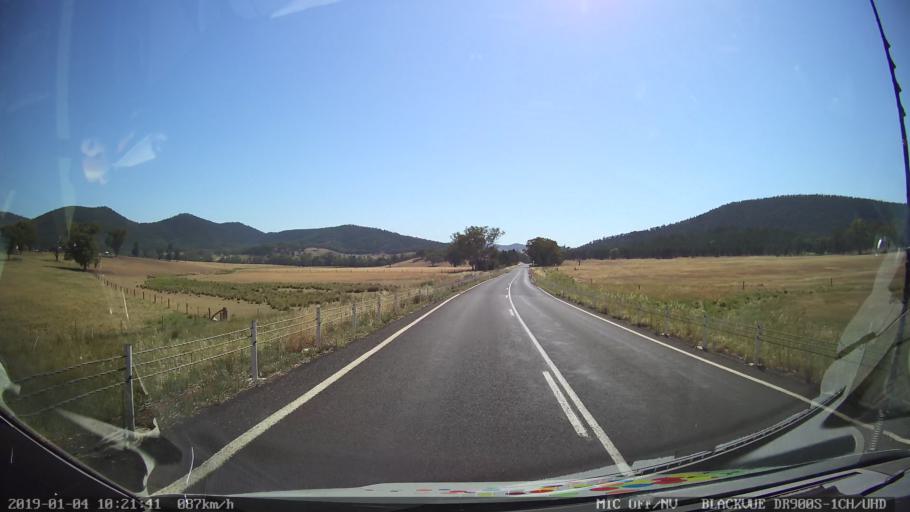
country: AU
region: New South Wales
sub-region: Cabonne
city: Canowindra
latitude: -33.3713
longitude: 148.5137
